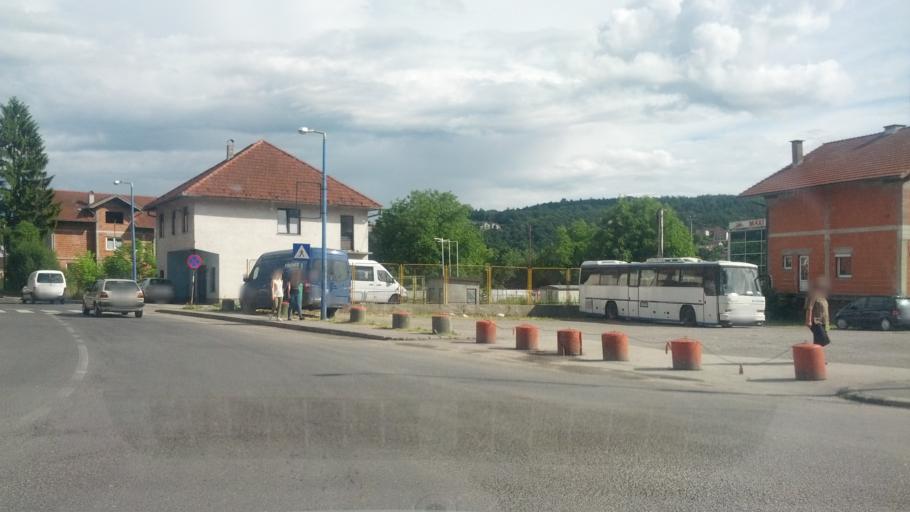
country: BA
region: Federation of Bosnia and Herzegovina
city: Bosanska Krupa
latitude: 44.8865
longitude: 16.1507
